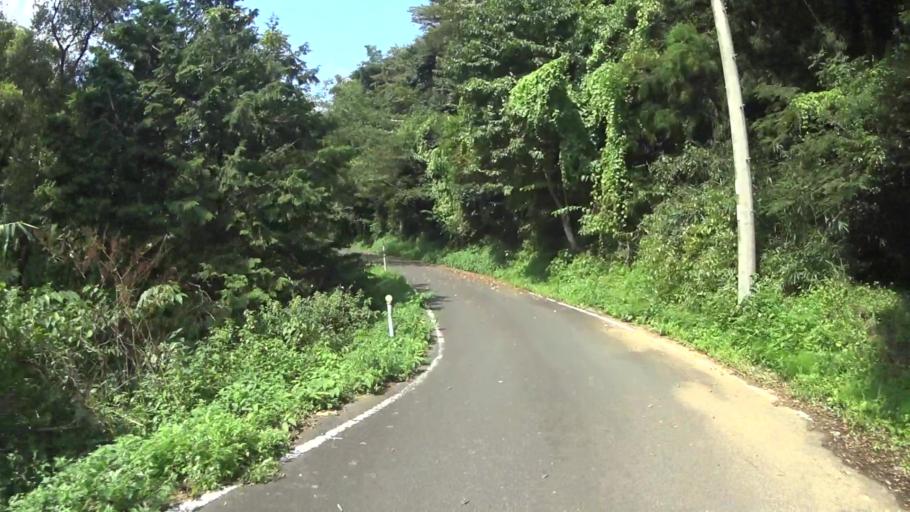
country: JP
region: Kyoto
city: Miyazu
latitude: 35.6563
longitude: 135.2498
